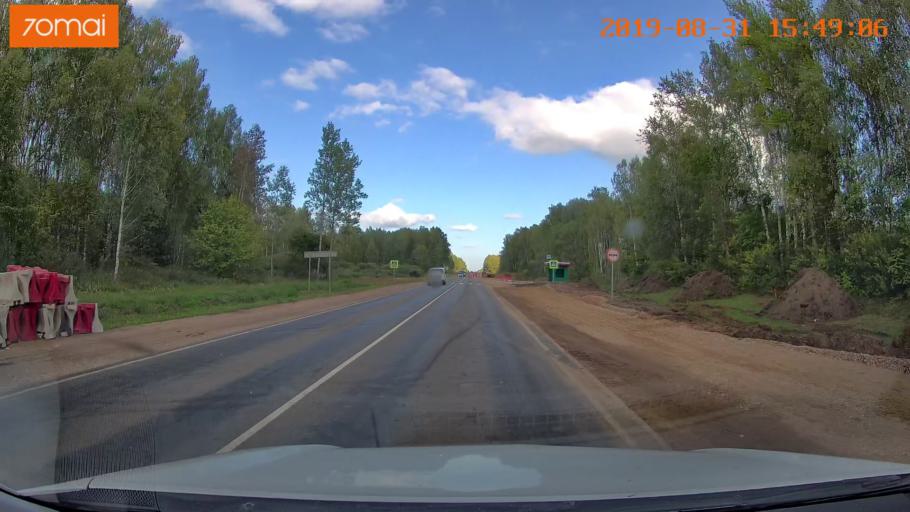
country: RU
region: Kaluga
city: Yukhnov
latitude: 54.6896
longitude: 35.0453
